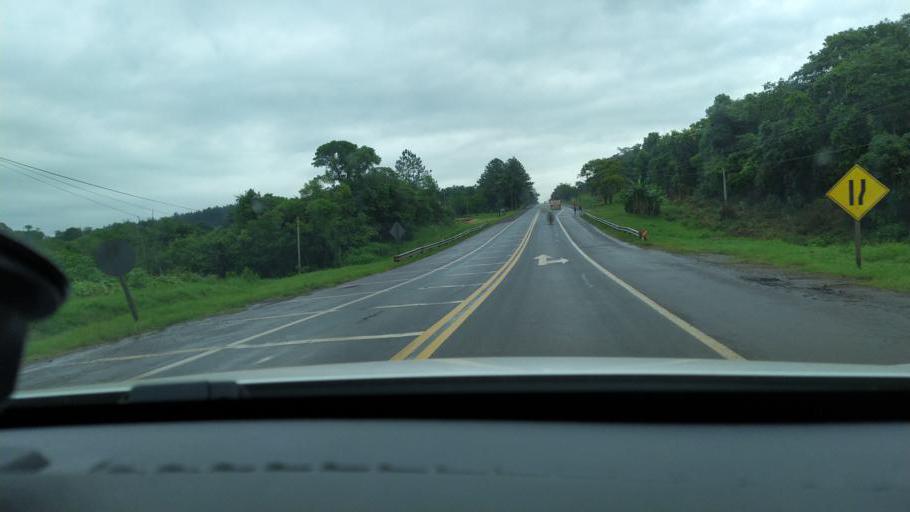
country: AR
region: Misiones
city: Garuhape
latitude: -26.8209
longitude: -54.9624
